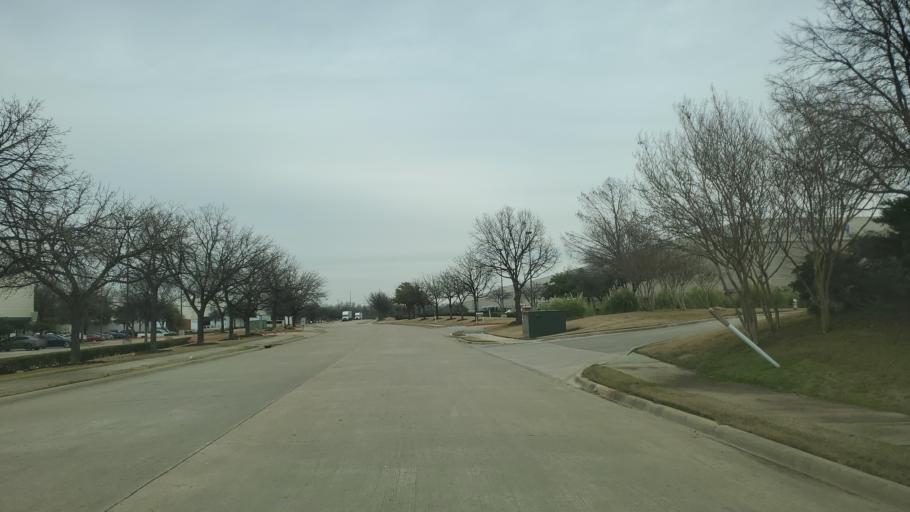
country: US
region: Texas
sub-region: Dallas County
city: Coppell
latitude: 32.9851
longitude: -97.0250
